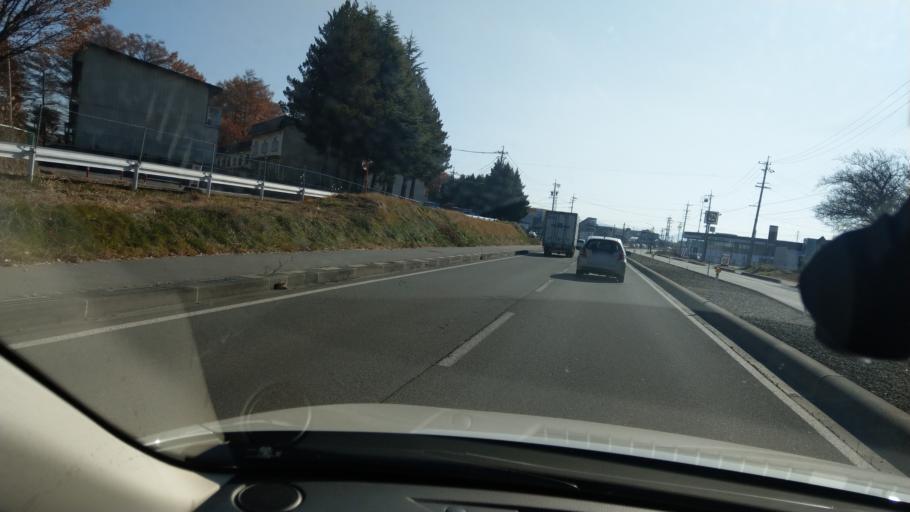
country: JP
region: Nagano
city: Komoro
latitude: 36.3027
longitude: 138.4640
